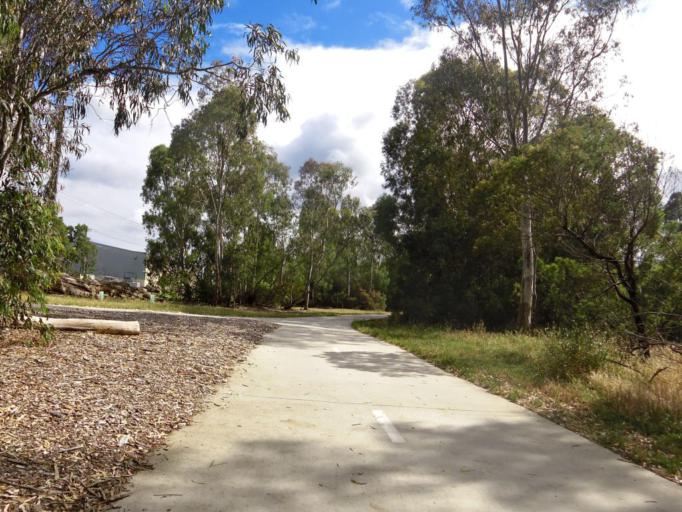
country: AU
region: Victoria
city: Heidelberg West
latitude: -37.7608
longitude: 145.0284
